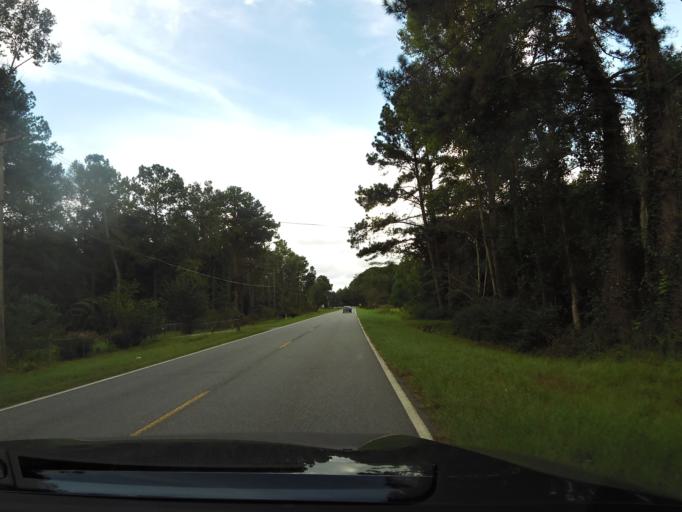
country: US
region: Georgia
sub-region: Liberty County
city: Midway
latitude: 31.8467
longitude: -81.4177
